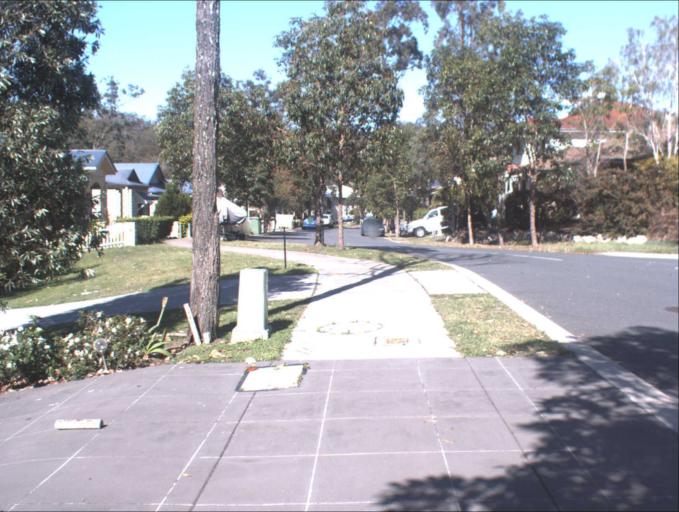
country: AU
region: Queensland
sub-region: Logan
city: Waterford West
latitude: -27.7112
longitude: 153.1542
